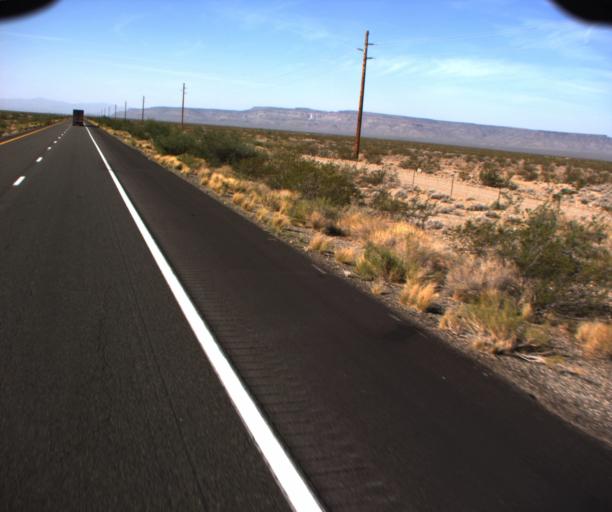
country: US
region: Arizona
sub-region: Mohave County
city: Kingman
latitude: 35.0009
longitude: -114.1369
